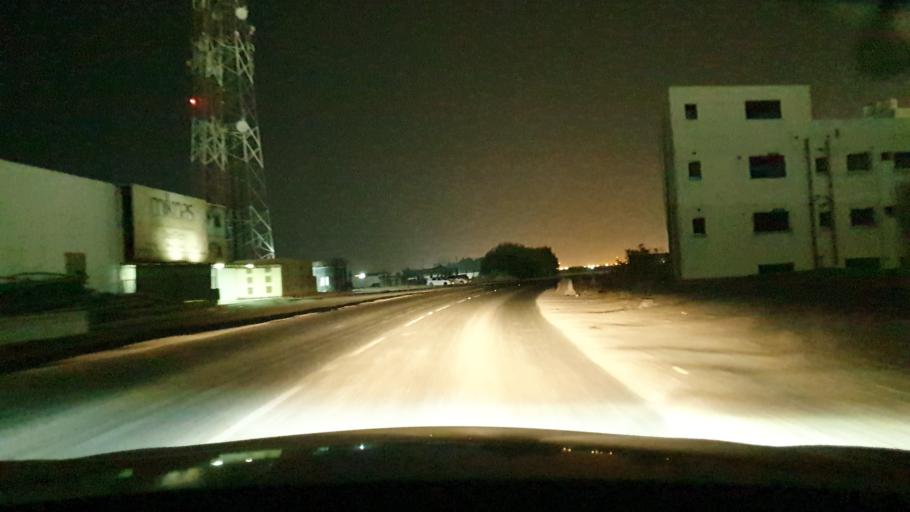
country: BH
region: Northern
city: Sitrah
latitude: 26.0964
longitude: 50.6150
